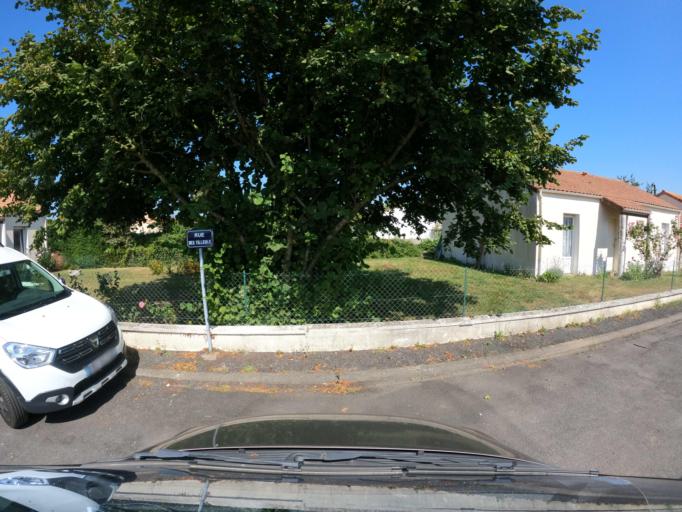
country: FR
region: Pays de la Loire
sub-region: Departement de la Loire-Atlantique
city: La Planche
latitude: 47.0173
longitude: -1.4289
